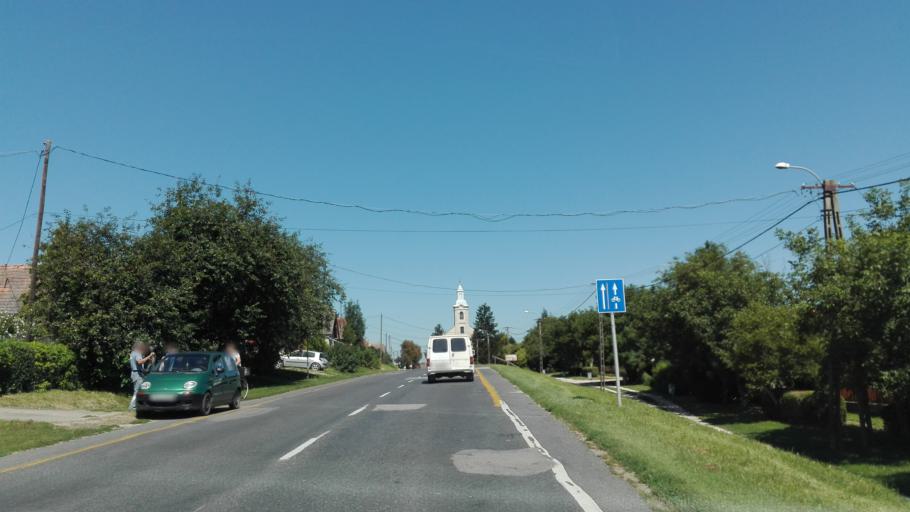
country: HU
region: Tolna
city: Simontornya
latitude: 46.7724
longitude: 18.5161
